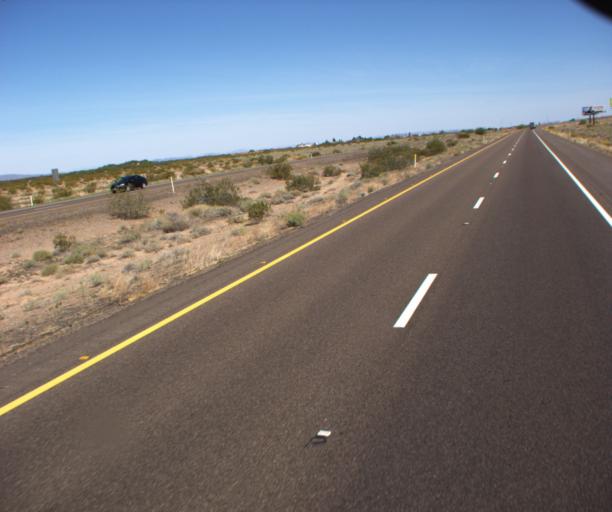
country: US
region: Arizona
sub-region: Yuma County
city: Wellton
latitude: 32.7948
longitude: -113.5514
